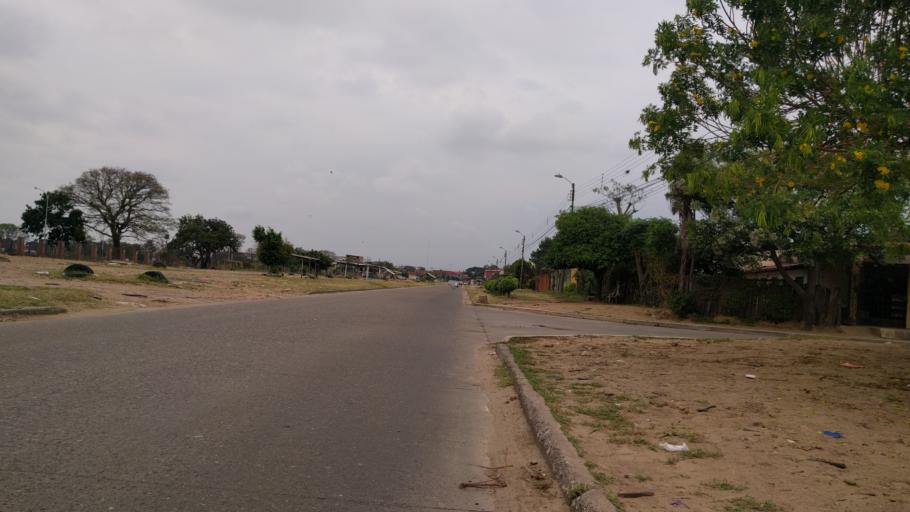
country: BO
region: Santa Cruz
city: Santa Cruz de la Sierra
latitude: -17.8262
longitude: -63.1984
